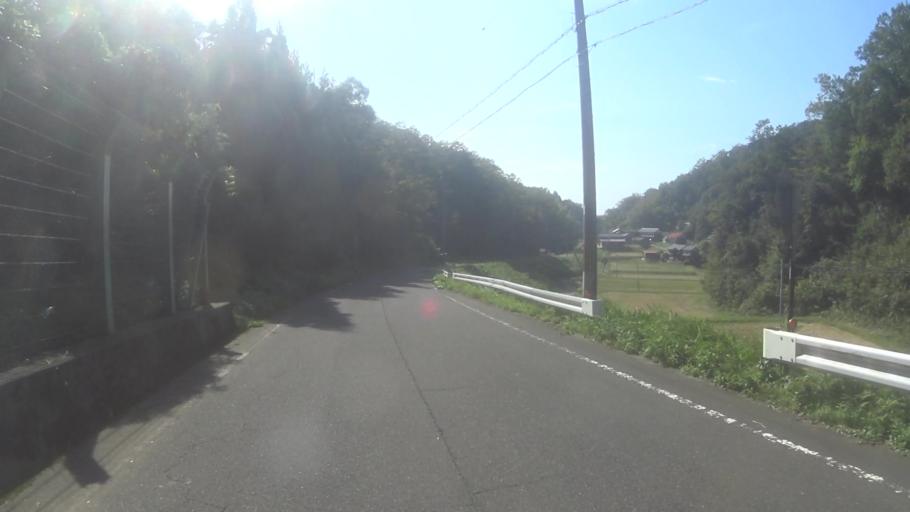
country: JP
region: Kyoto
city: Miyazu
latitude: 35.6931
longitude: 135.1377
